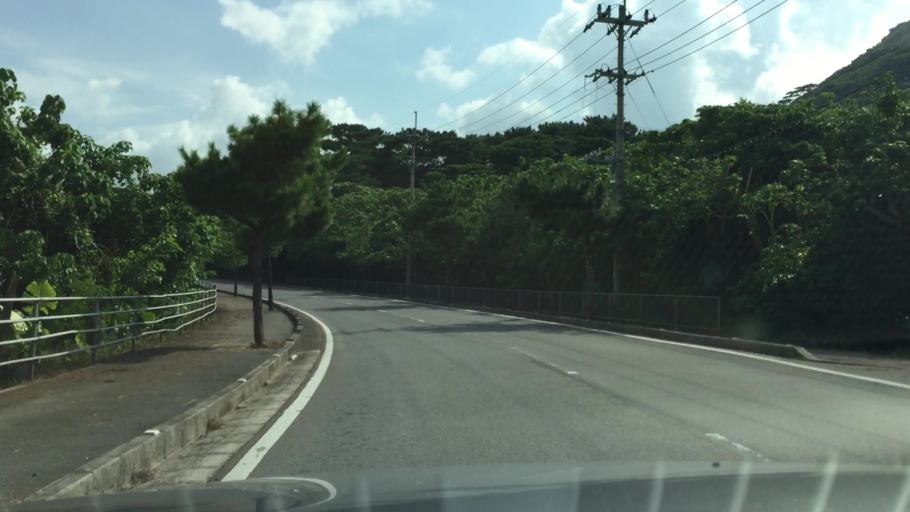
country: JP
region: Okinawa
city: Ishigaki
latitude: 24.4864
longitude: 124.2710
